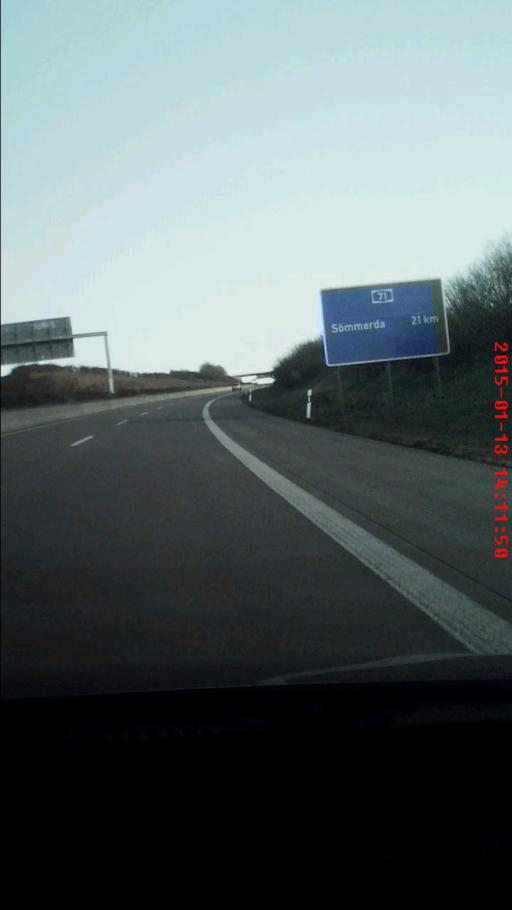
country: DE
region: Thuringia
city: Kleinmolsen
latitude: 51.0417
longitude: 11.0677
